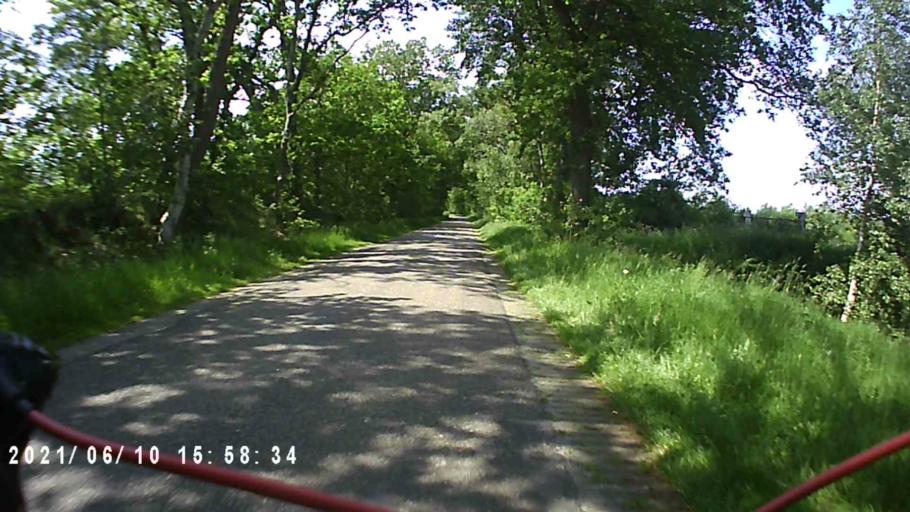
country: NL
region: Friesland
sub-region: Gemeente Achtkarspelen
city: Kootstertille
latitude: 53.1921
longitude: 6.0900
